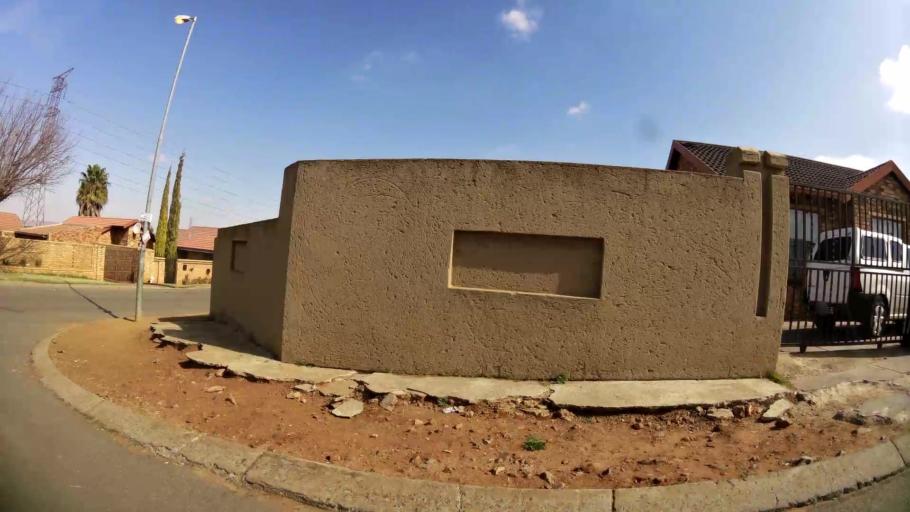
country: ZA
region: Gauteng
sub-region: City of Johannesburg Metropolitan Municipality
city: Soweto
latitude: -26.2653
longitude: 27.8843
